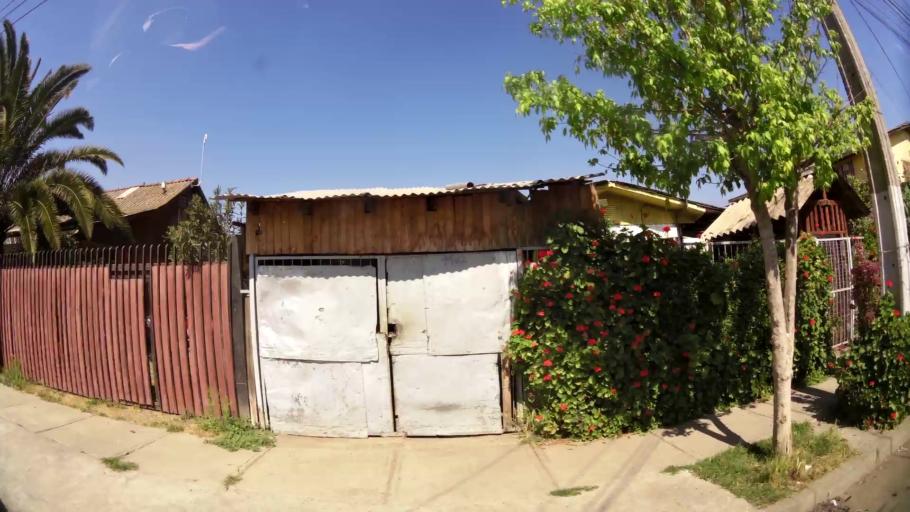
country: CL
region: Santiago Metropolitan
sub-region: Provincia de Talagante
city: Penaflor
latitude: -33.5689
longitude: -70.7997
